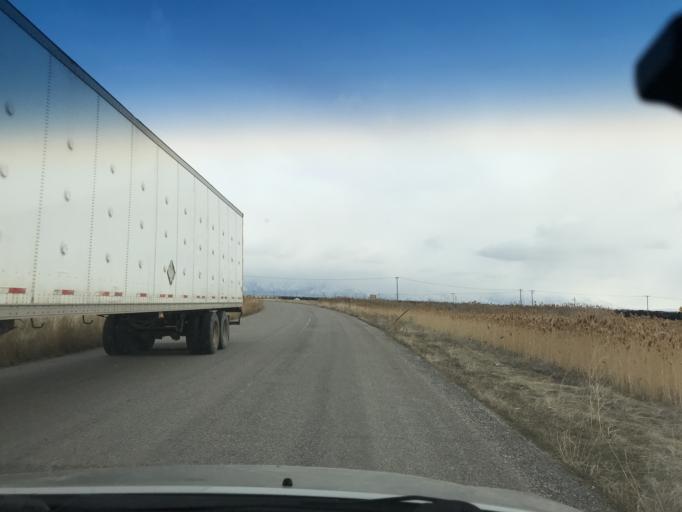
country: US
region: Utah
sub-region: Salt Lake County
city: Magna
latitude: 40.7721
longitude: -112.0594
